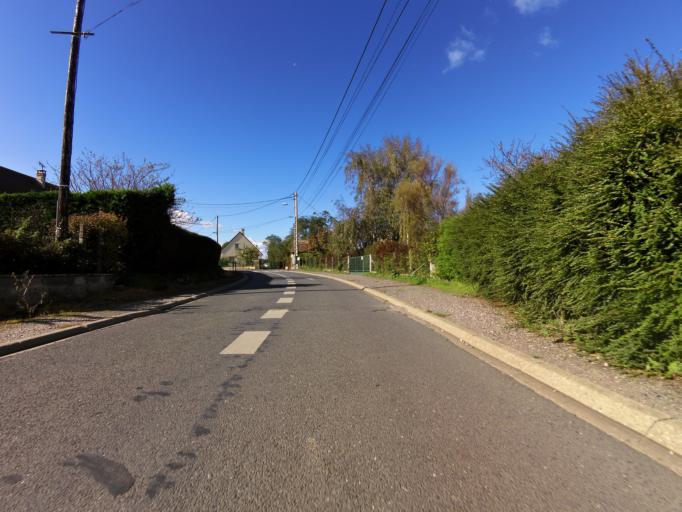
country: FR
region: Lower Normandy
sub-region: Departement du Calvados
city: Canon
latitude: 49.0482
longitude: -0.1355
